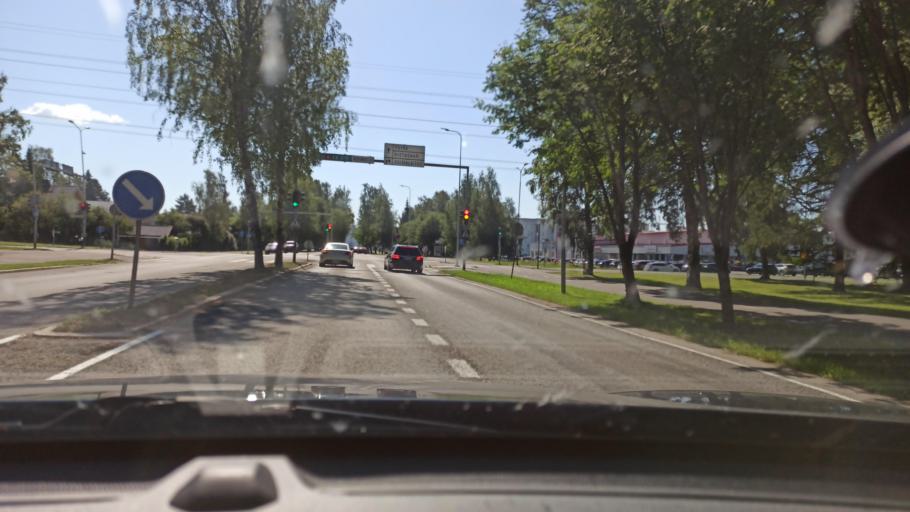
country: FI
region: Northern Ostrobothnia
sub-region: Oulu
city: Oulu
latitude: 65.0388
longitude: 25.4424
